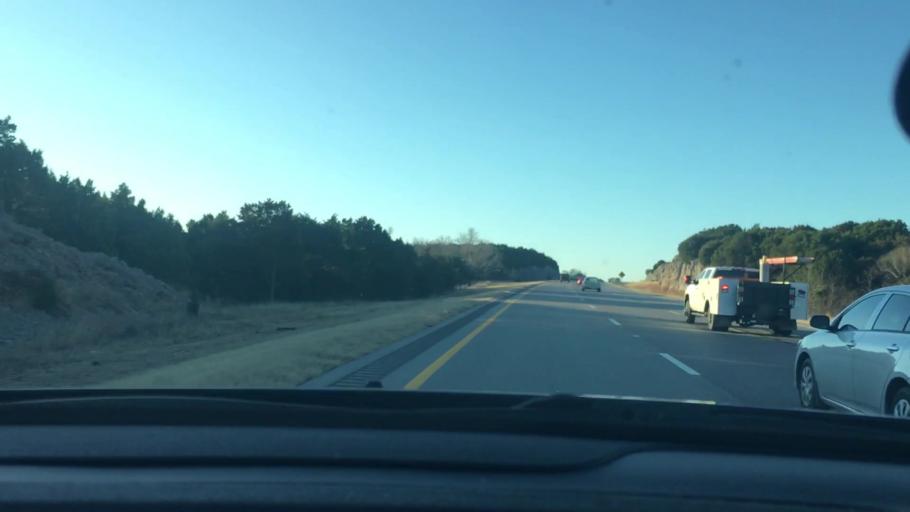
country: US
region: Oklahoma
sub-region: Murray County
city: Davis
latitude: 34.4261
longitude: -97.1340
